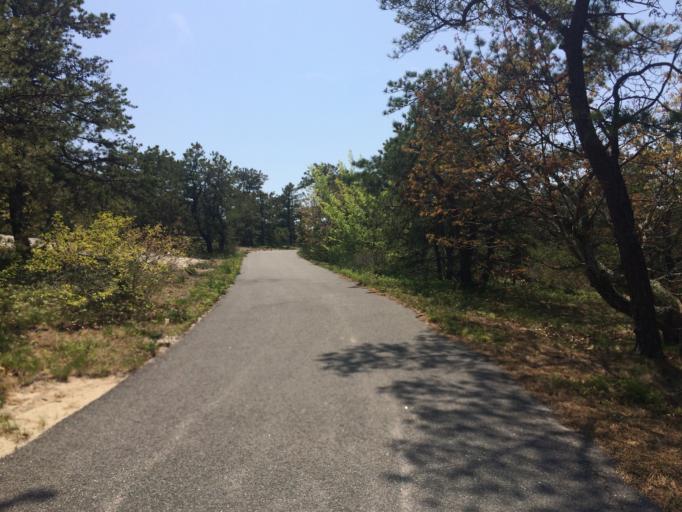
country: US
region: Massachusetts
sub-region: Barnstable County
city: Provincetown
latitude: 42.0735
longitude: -70.2118
